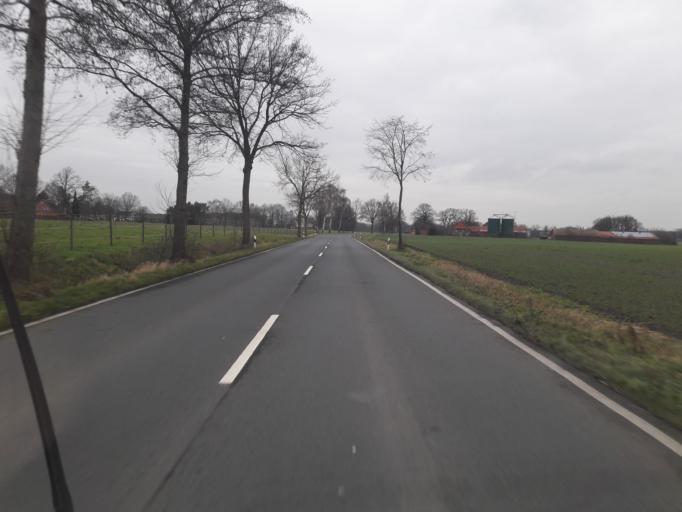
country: DE
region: Lower Saxony
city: Warmsen
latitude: 52.3714
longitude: 8.8467
